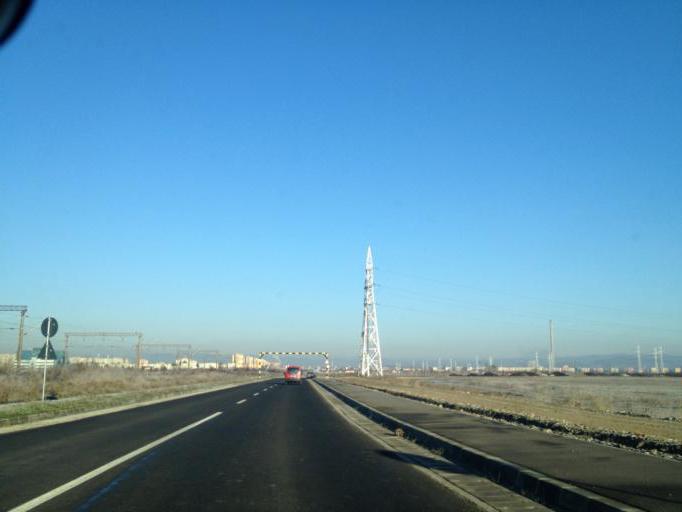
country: RO
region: Brasov
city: Brasov
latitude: 45.6288
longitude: 25.6483
